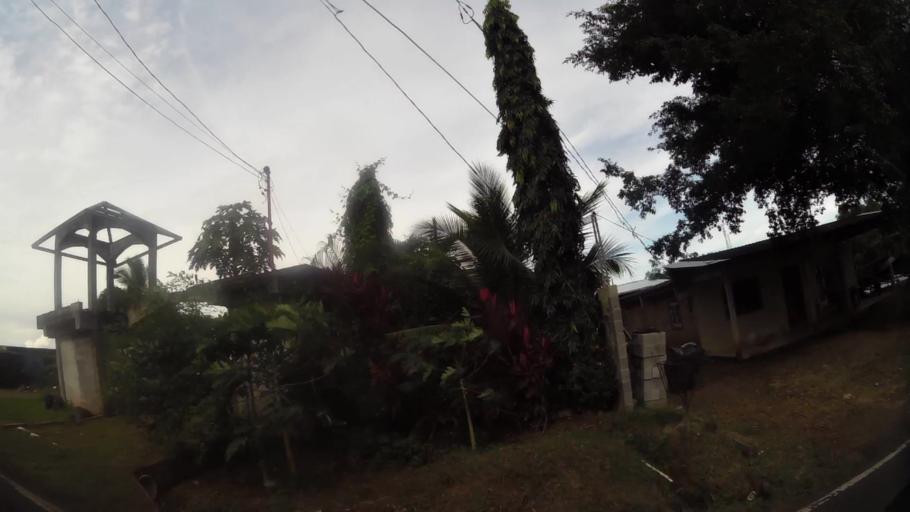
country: PA
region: Panama
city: El Coco
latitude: 8.8748
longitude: -79.8052
